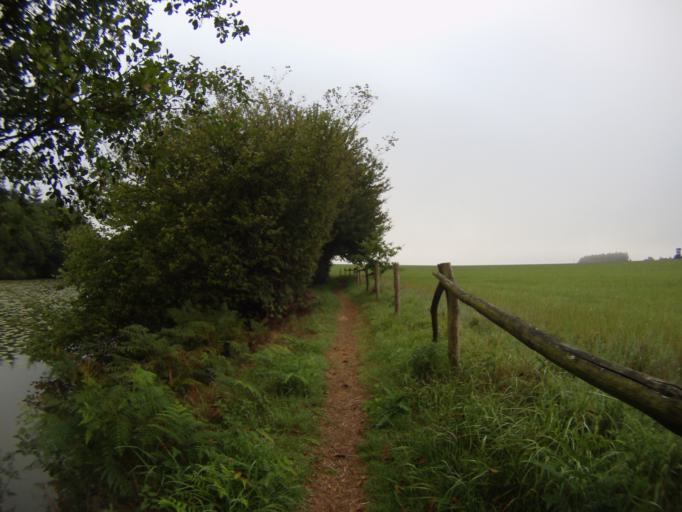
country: FR
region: Brittany
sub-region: Departement d'Ille-et-Vilaine
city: Chanteloup
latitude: 47.9723
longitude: -1.6117
